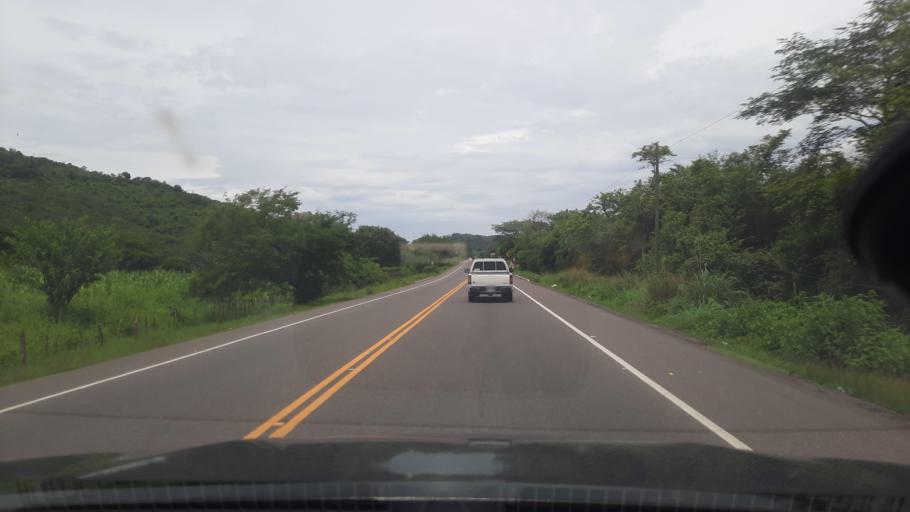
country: HN
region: Valle
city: Langue
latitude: 13.5878
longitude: -87.6929
